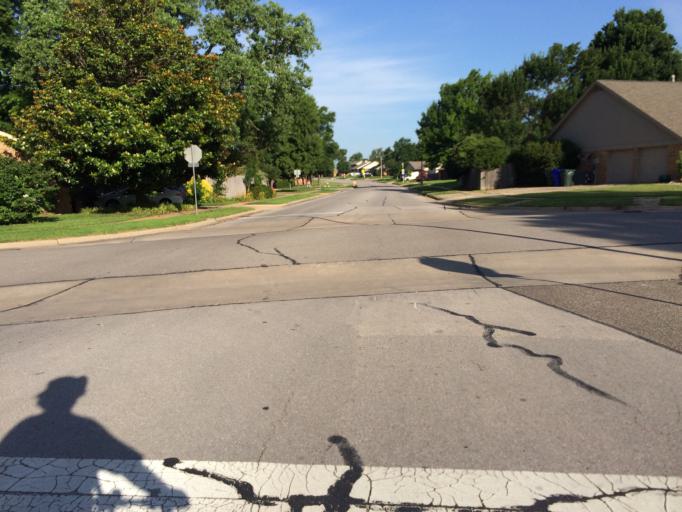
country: US
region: Oklahoma
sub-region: Cleveland County
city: Norman
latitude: 35.2236
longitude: -97.5000
